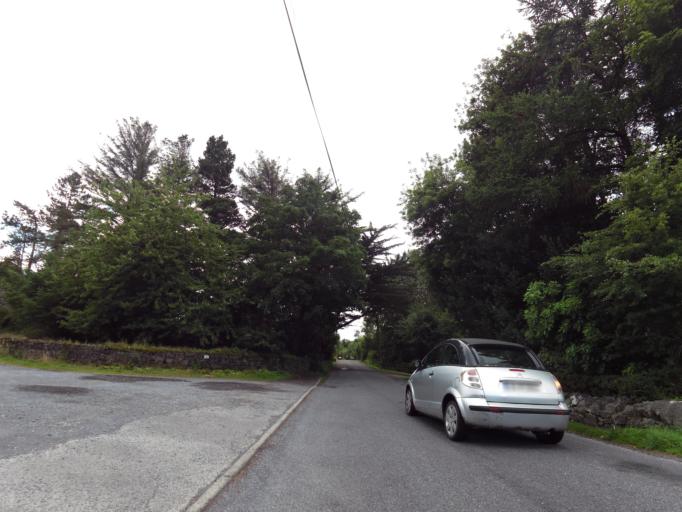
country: IE
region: Connaught
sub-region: County Galway
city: Oughterard
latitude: 53.4225
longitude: -9.3285
